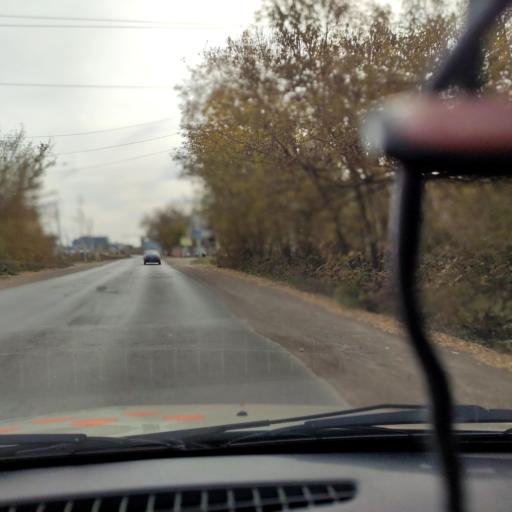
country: RU
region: Bashkortostan
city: Ufa
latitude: 54.5751
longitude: 55.9191
